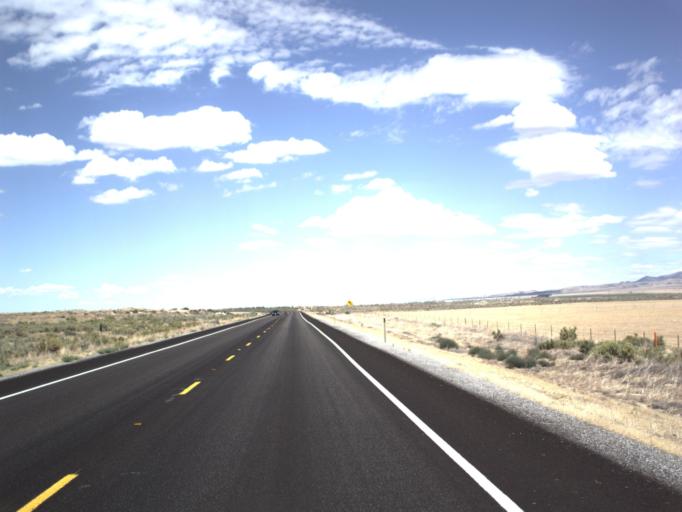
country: US
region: Utah
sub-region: Millard County
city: Fillmore
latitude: 39.1278
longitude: -112.3595
